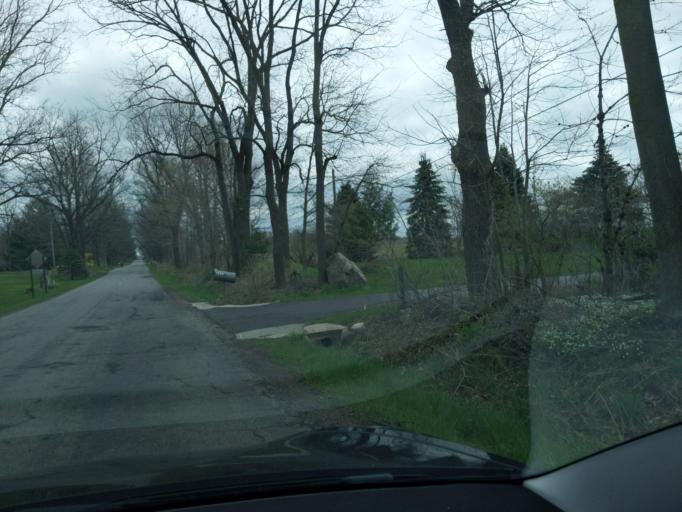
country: US
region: Michigan
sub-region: Ingham County
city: Holt
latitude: 42.5675
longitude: -84.5606
